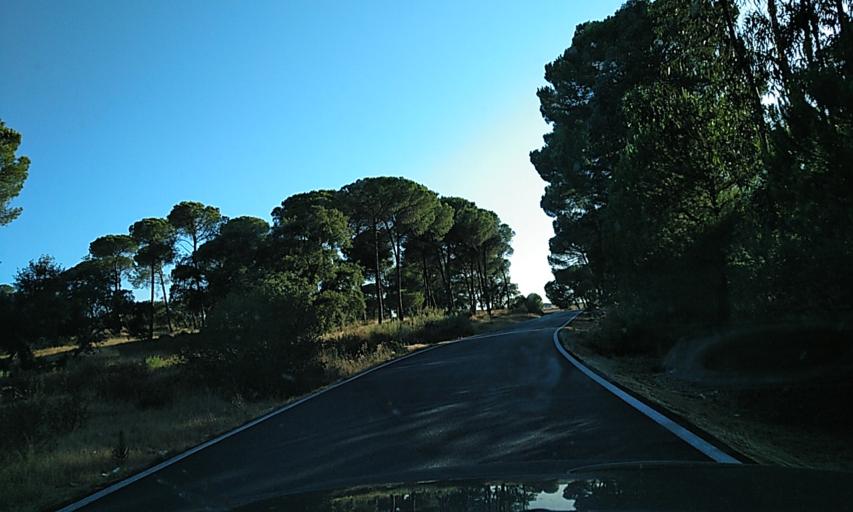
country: ES
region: Andalusia
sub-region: Provincia de Huelva
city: San Bartolome de la Torre
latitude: 37.3962
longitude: -7.1299
